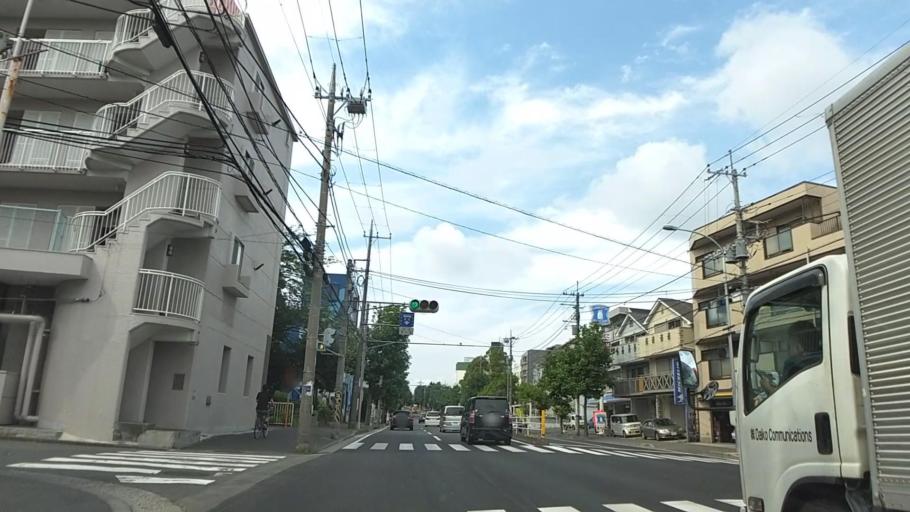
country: JP
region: Kanagawa
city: Yokohama
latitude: 35.5214
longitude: 139.6376
